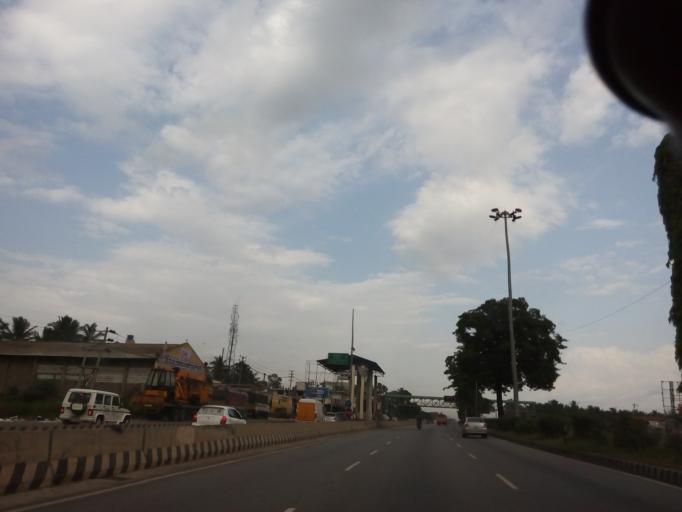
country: IN
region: Karnataka
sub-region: Bangalore Rural
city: Nelamangala
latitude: 13.0555
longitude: 77.4784
